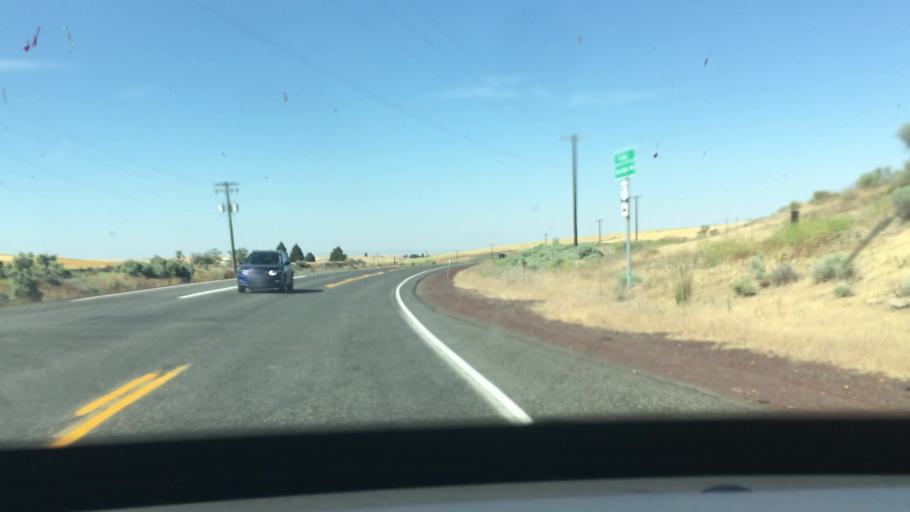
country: US
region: Oregon
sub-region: Sherman County
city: Moro
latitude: 45.4530
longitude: -120.7514
